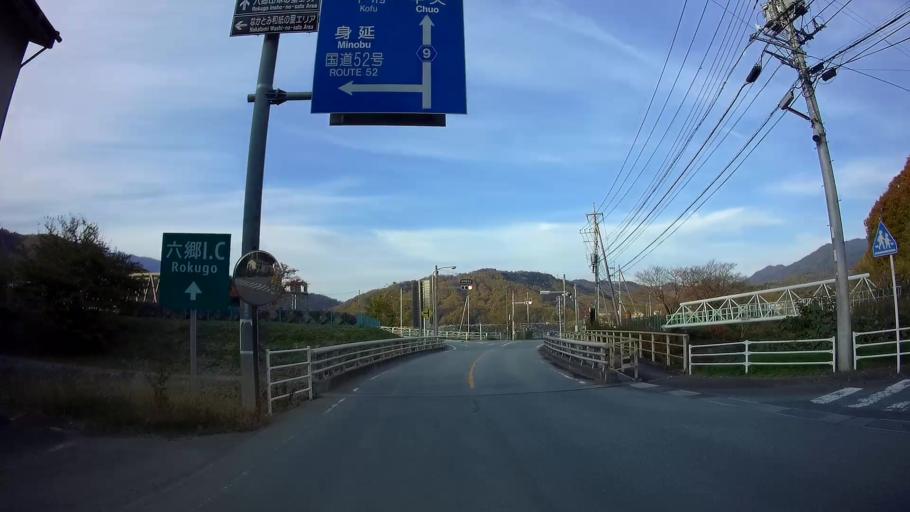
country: JP
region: Yamanashi
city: Ryuo
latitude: 35.4836
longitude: 138.4560
